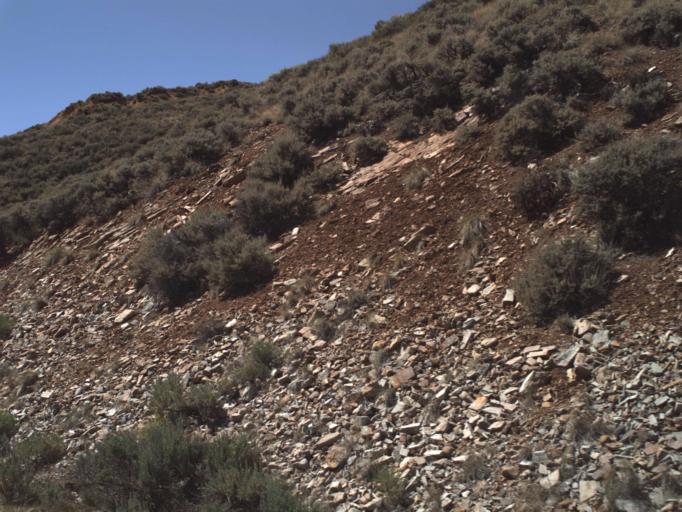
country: US
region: Utah
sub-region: Rich County
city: Randolph
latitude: 41.4801
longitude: -111.3502
